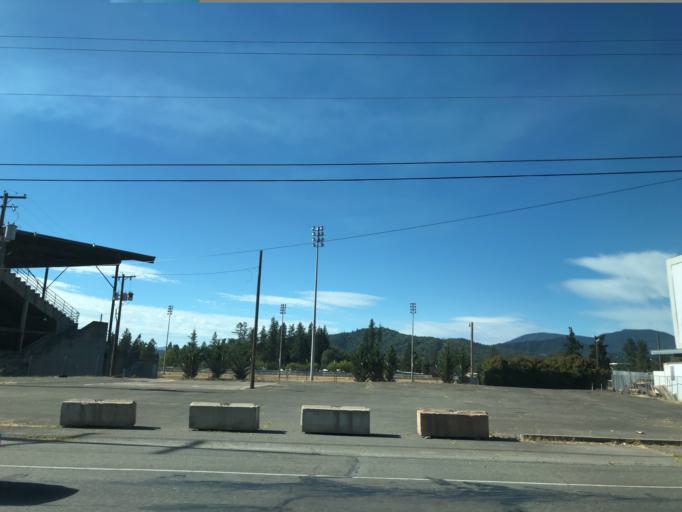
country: US
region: Oregon
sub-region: Josephine County
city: Grants Pass
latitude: 42.4227
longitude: -123.3448
